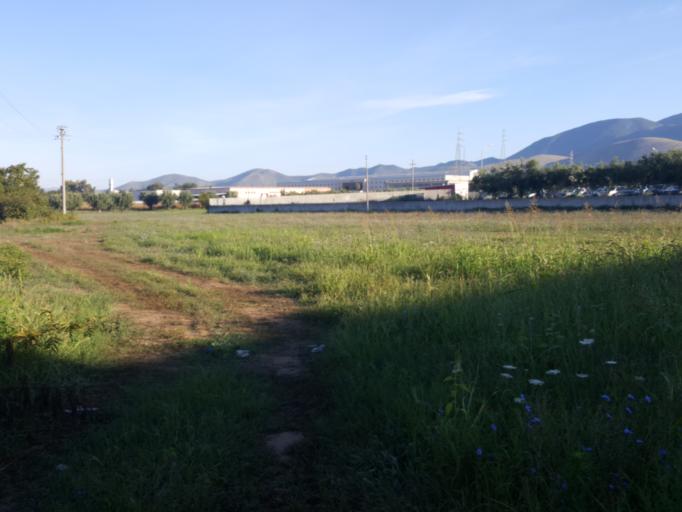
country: IT
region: Campania
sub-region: Provincia di Caserta
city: Pignataro Maggiore
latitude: 41.1609
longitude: 14.1613
